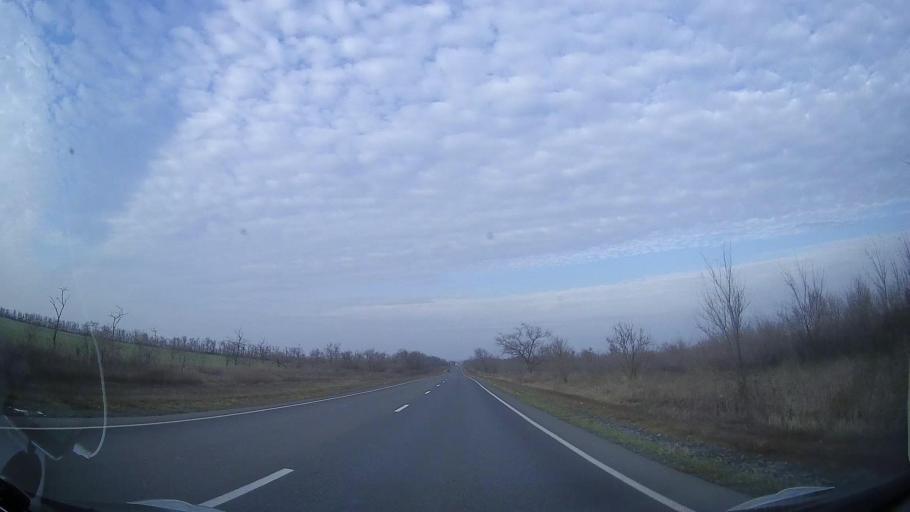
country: RU
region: Rostov
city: Bagayevskaya
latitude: 47.1501
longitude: 40.2765
